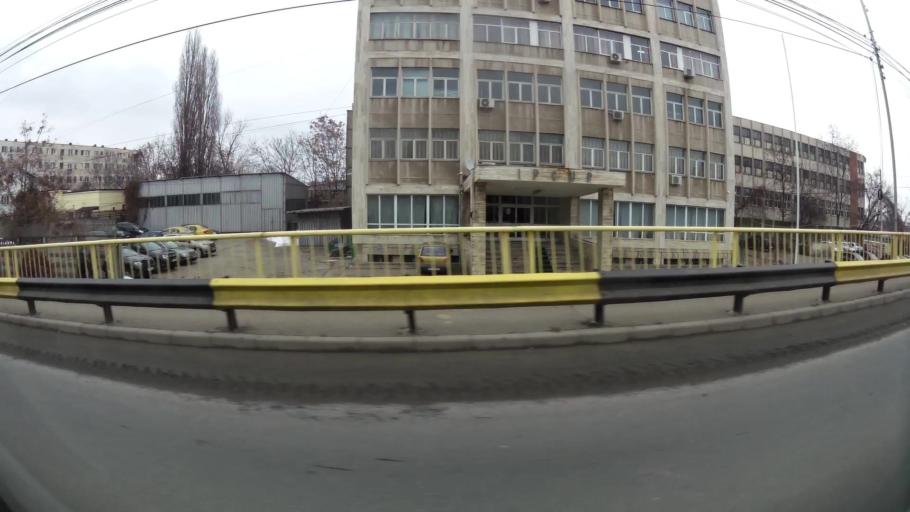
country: RO
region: Prahova
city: Ploiesti
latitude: 44.9281
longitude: 26.0329
